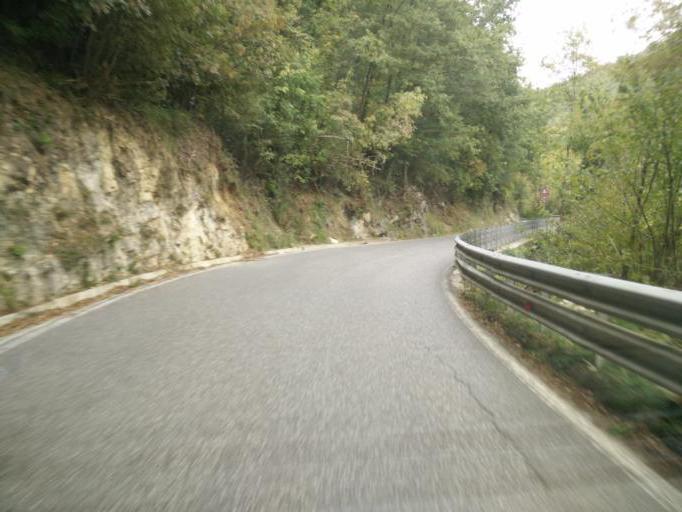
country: IT
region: Tuscany
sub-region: Provincia di Massa-Carrara
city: Casola in Lunigiana
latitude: 44.1912
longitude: 10.1335
